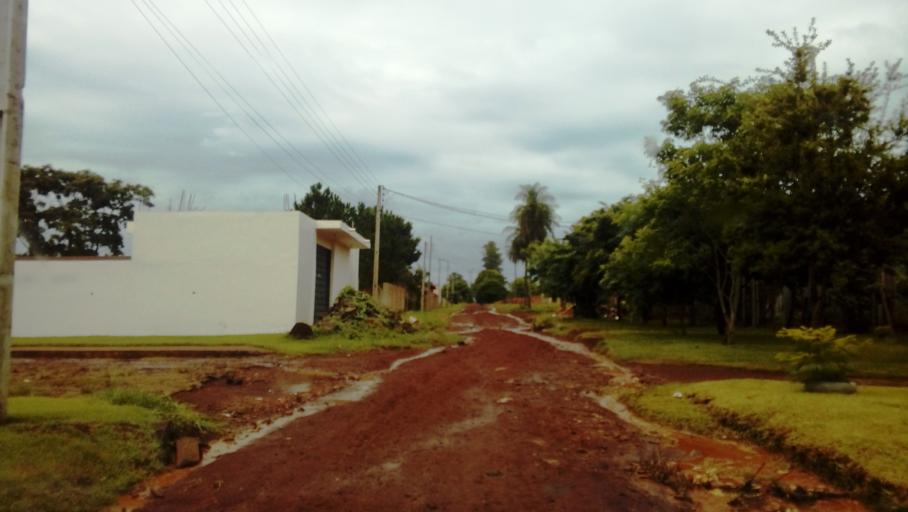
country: PY
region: Alto Parana
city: Ciudad del Este
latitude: -25.4234
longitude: -54.6409
